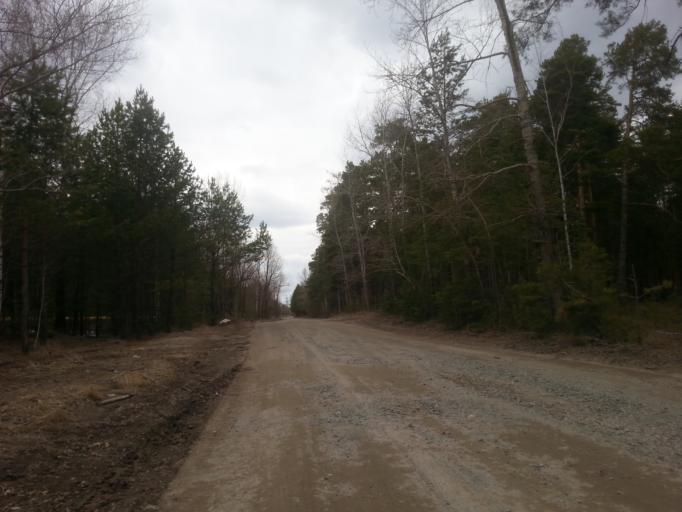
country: RU
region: Altai Krai
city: Yuzhnyy
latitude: 53.2801
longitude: 83.7350
